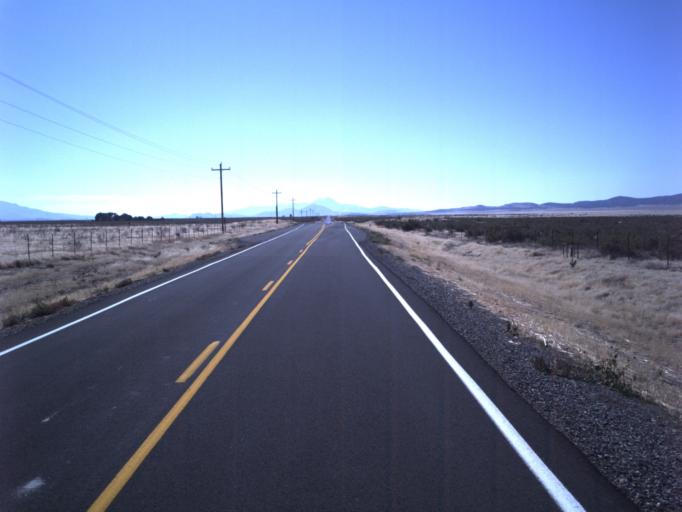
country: US
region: Utah
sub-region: Tooele County
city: Grantsville
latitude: 40.3586
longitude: -112.7458
